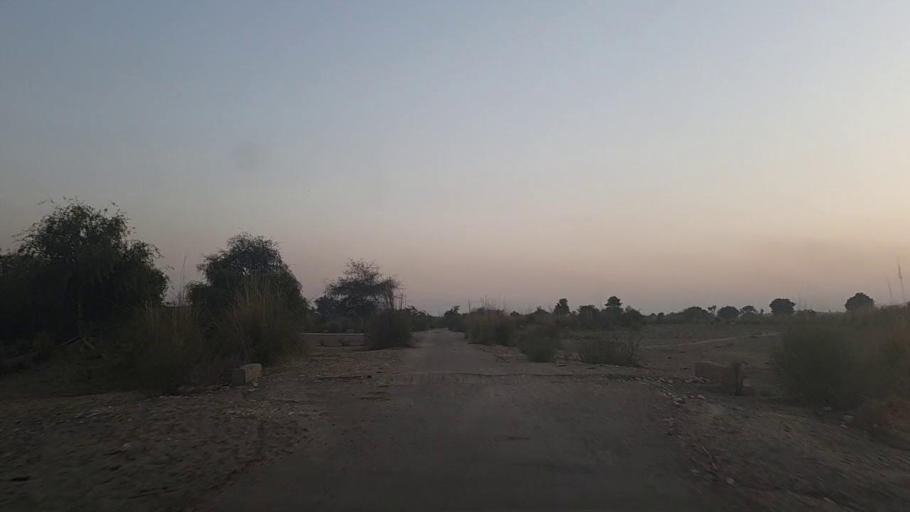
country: PK
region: Sindh
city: Jam Sahib
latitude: 26.3905
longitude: 68.8094
